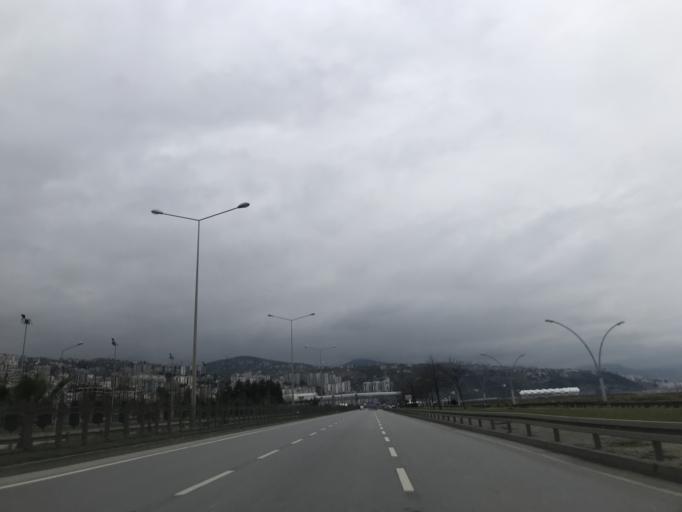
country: TR
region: Trabzon
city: Trabzon
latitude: 40.9994
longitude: 39.6795
